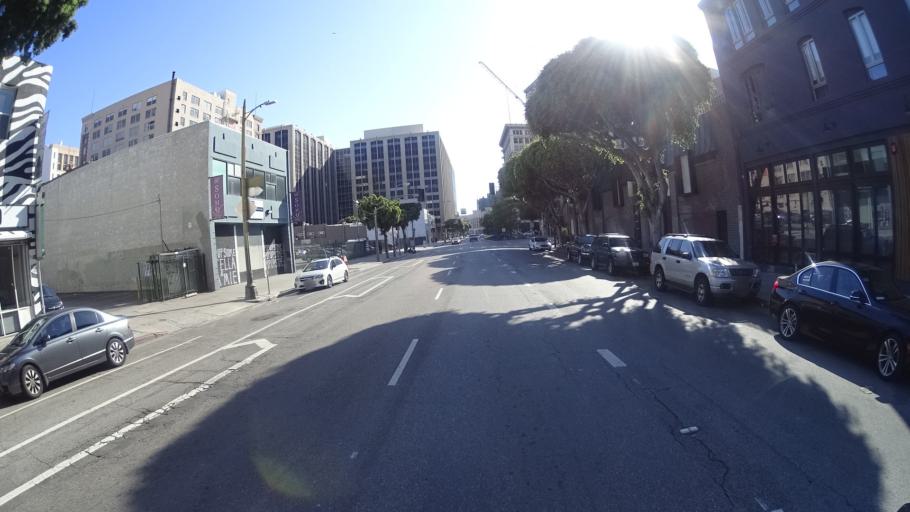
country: US
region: California
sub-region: Los Angeles County
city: Los Angeles
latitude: 34.0424
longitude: -118.2538
